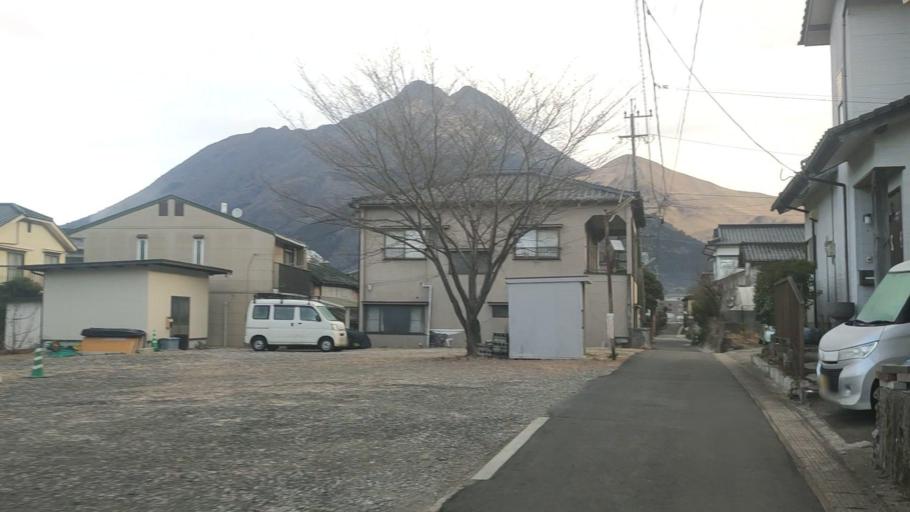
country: JP
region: Oita
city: Beppu
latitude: 33.2577
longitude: 131.3578
